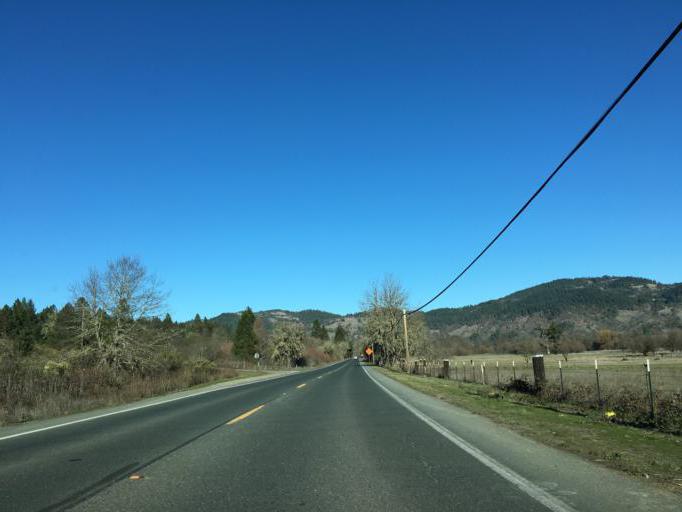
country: US
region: California
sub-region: Mendocino County
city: Brooktrails
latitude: 39.4419
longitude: -123.3546
